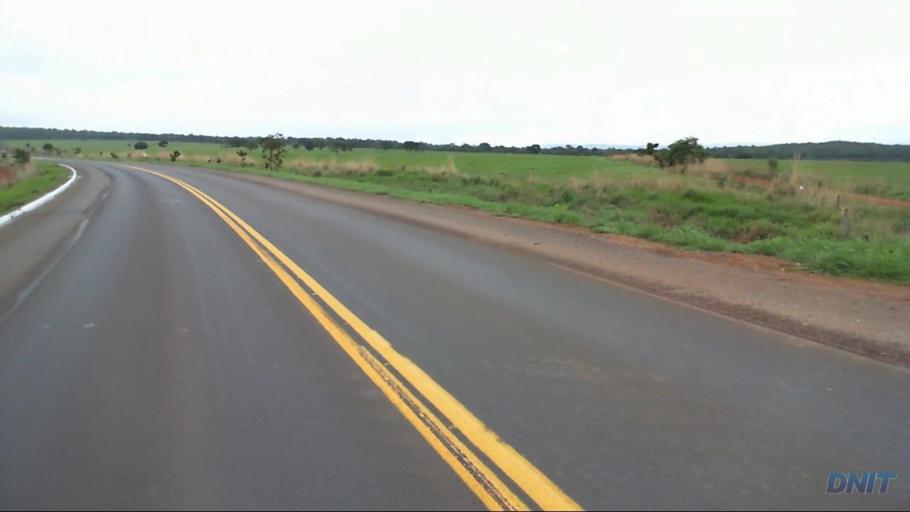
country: BR
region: Goias
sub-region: Padre Bernardo
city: Padre Bernardo
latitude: -15.1731
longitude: -48.3908
